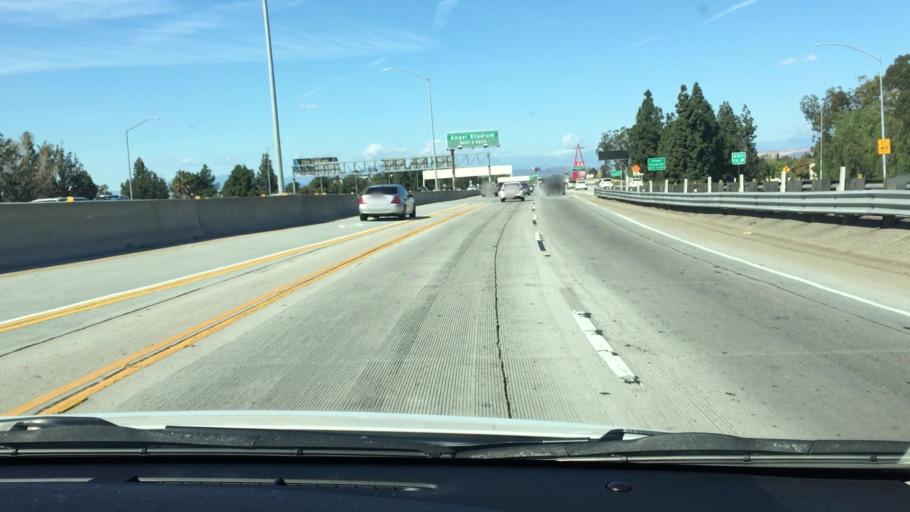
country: US
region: California
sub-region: Orange County
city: Orange
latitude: 33.7842
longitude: -117.8799
